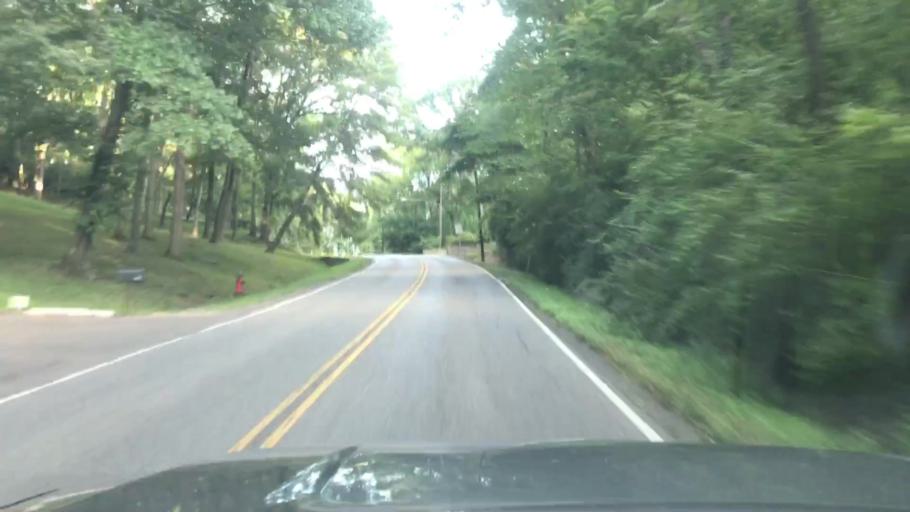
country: US
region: Tennessee
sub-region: Davidson County
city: Belle Meade
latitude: 36.1336
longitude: -86.8718
